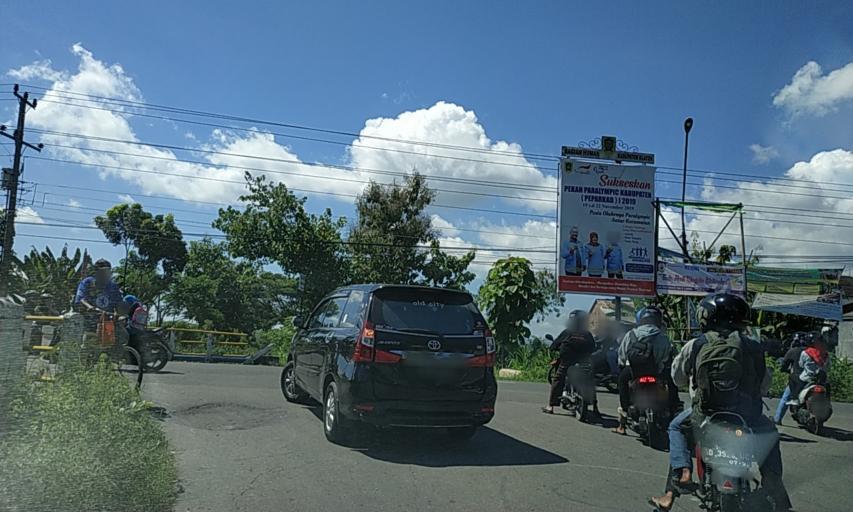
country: ID
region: Central Java
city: Trucuk
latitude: -7.7340
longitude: 110.7014
